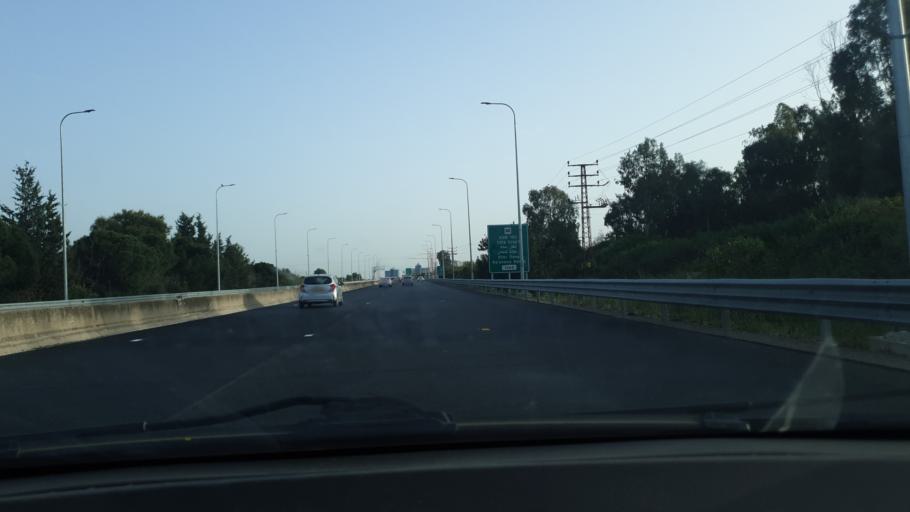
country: IL
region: Central District
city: Ra'anana
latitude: 32.2139
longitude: 34.8835
